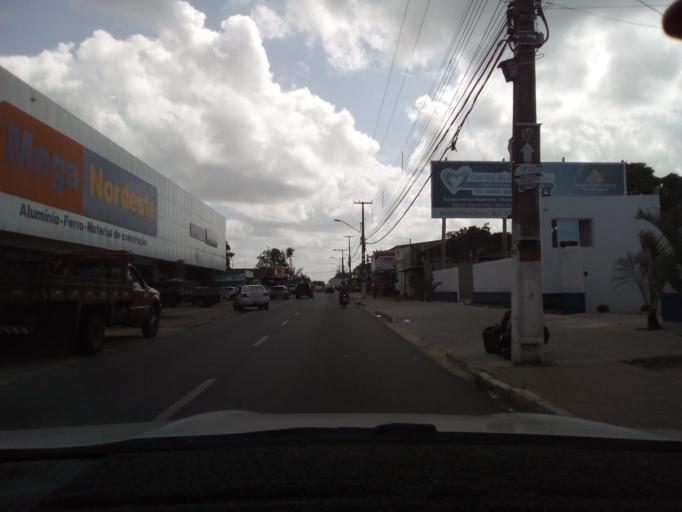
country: BR
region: Paraiba
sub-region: Bayeux
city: Bayeux
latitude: -7.1209
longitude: -34.9080
